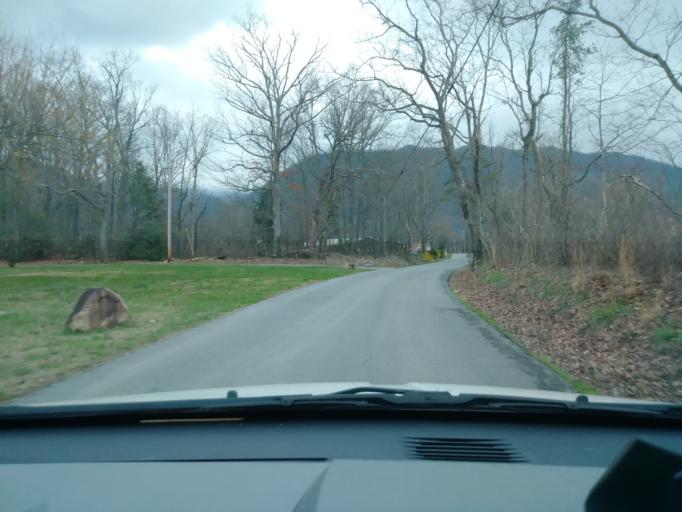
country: US
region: Tennessee
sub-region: Greene County
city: Tusculum
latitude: 36.0792
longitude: -82.7247
